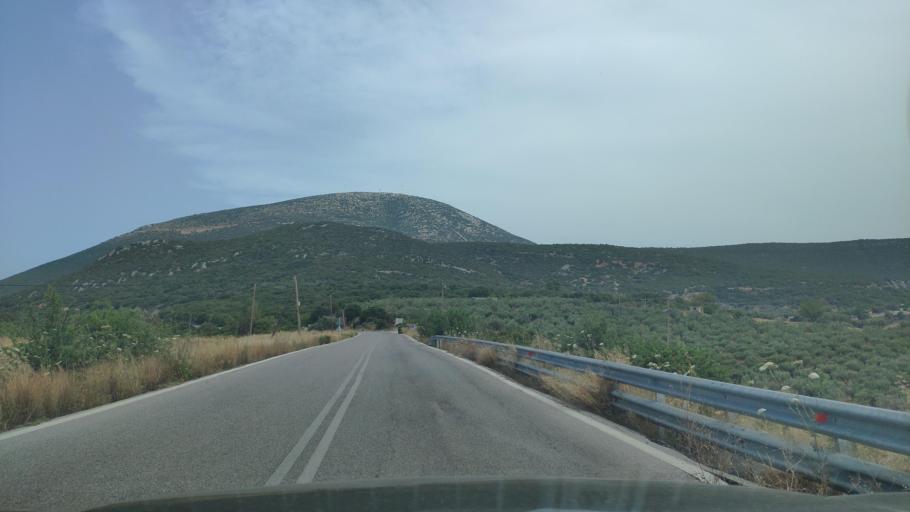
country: GR
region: Peloponnese
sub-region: Nomos Argolidos
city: Didyma
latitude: 37.5123
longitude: 23.1762
